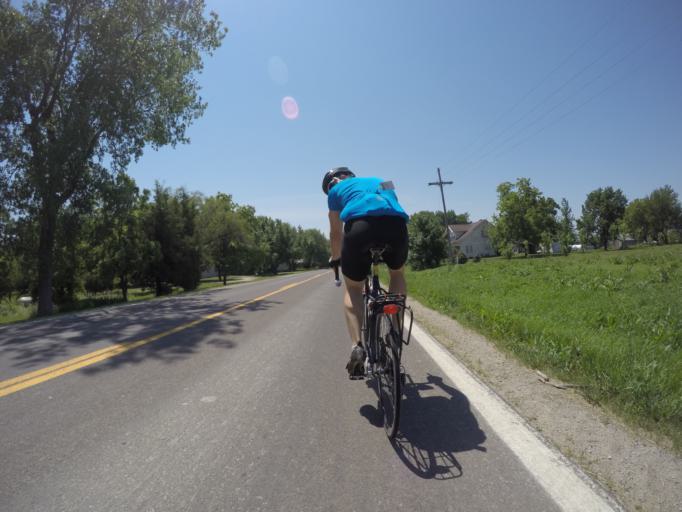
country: US
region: Nebraska
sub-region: Pawnee County
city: Pawnee City
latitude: 40.0378
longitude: -96.0482
